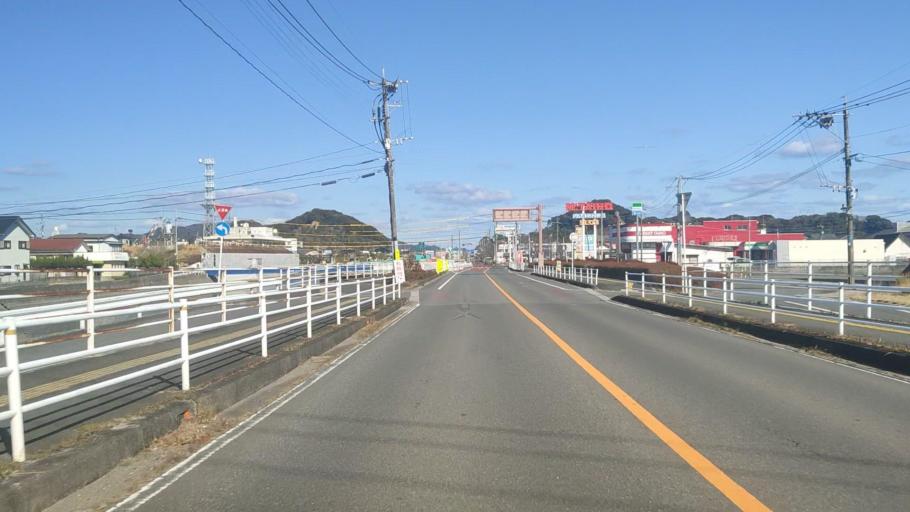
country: JP
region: Oita
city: Saiki
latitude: 32.9508
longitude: 131.9049
